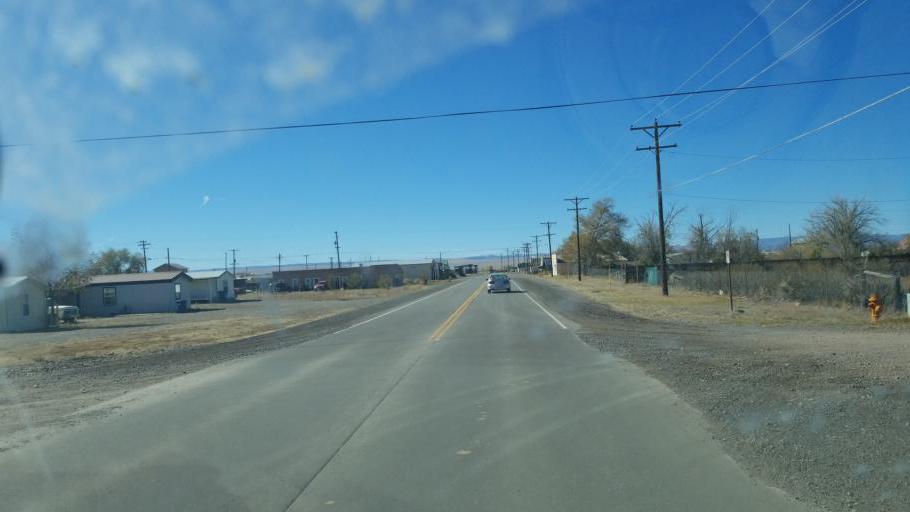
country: US
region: Colorado
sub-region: Conejos County
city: Conejos
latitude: 37.1743
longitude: -105.9850
